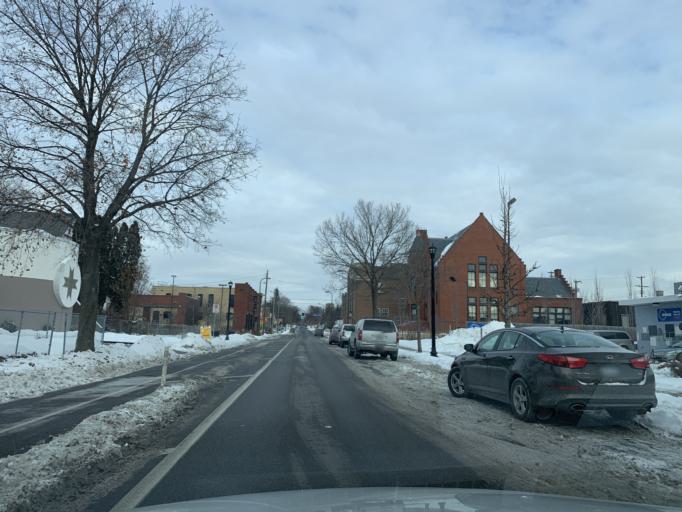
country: US
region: Minnesota
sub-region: Hennepin County
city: Minneapolis
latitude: 44.9977
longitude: -93.2941
